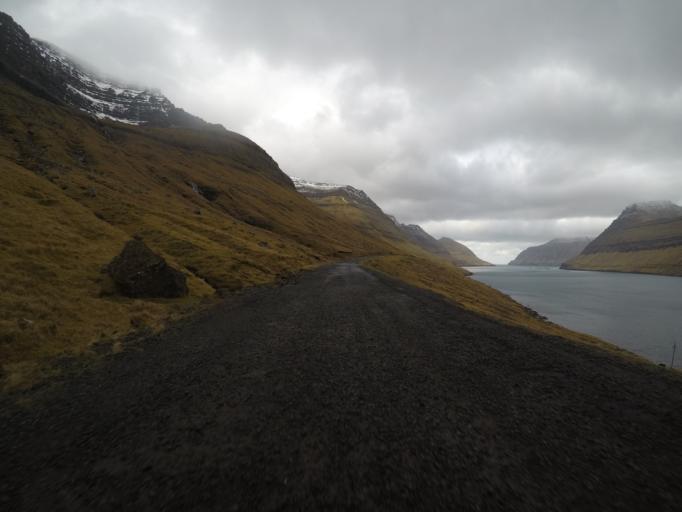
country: FO
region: Nordoyar
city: Klaksvik
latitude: 62.3103
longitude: -6.5463
